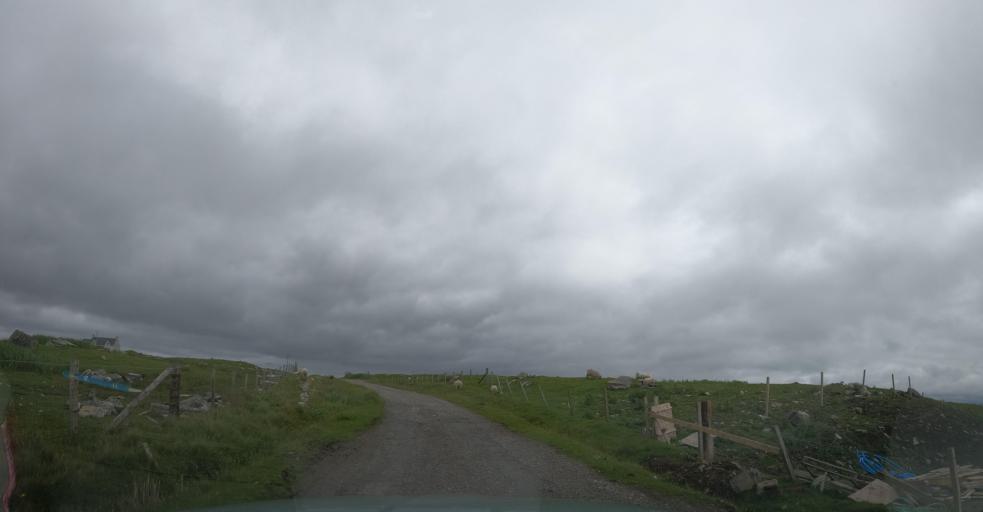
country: GB
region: Scotland
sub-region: Eilean Siar
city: Isle of North Uist
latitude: 57.5478
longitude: -7.3526
